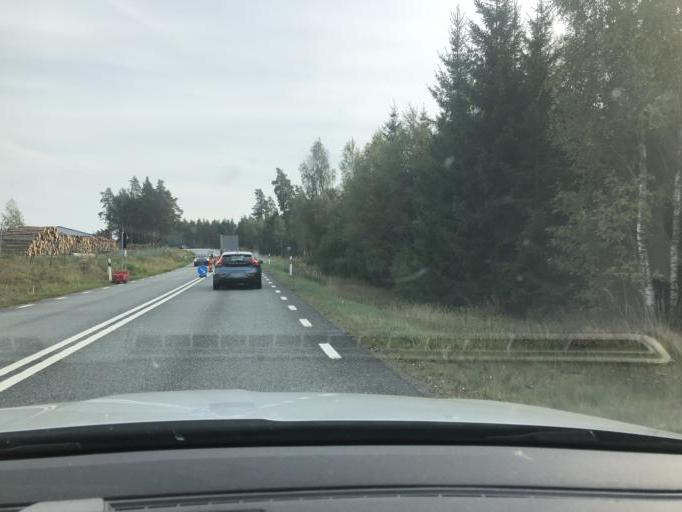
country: SE
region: Joenkoeping
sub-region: Vetlanda Kommun
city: Ekenassjon
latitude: 57.5556
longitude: 14.9821
